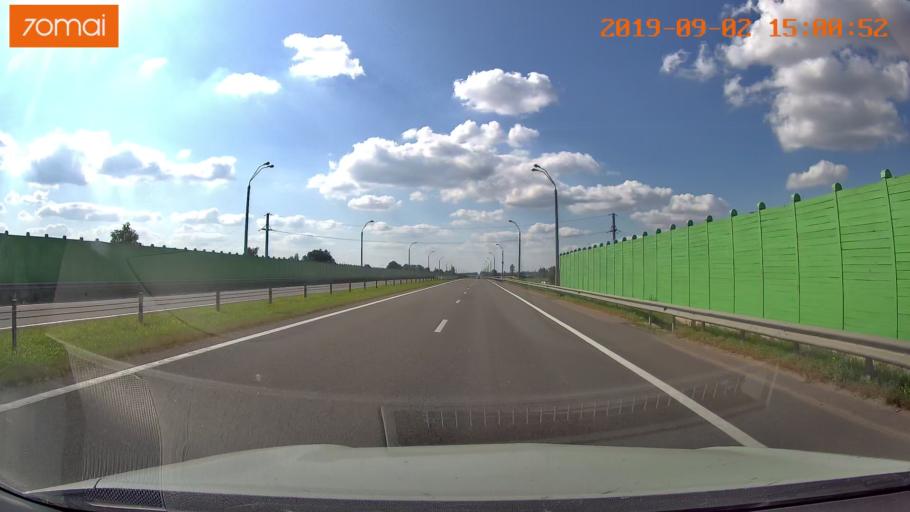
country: BY
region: Mogilev
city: Vishow
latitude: 53.9784
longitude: 30.0641
